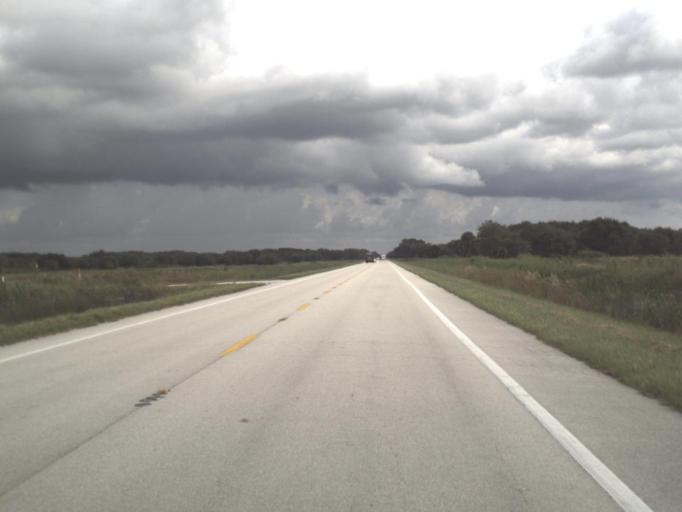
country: US
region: Florida
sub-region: Hendry County
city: Port LaBelle
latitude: 26.8535
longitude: -81.3774
